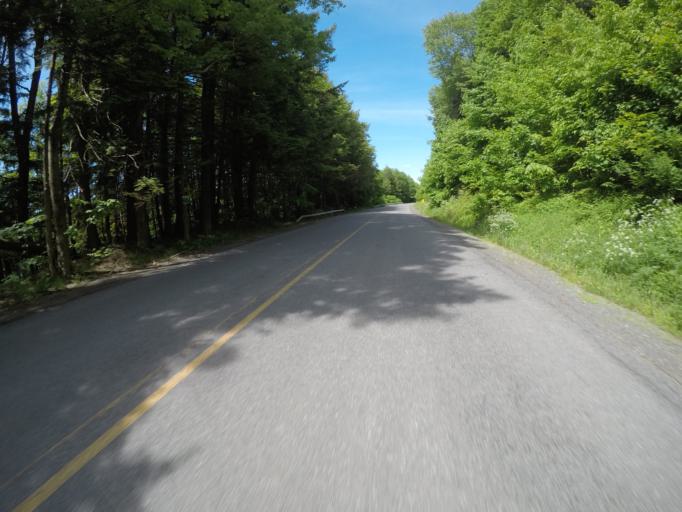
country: US
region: New York
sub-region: Delaware County
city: Delhi
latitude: 42.1041
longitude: -74.8252
